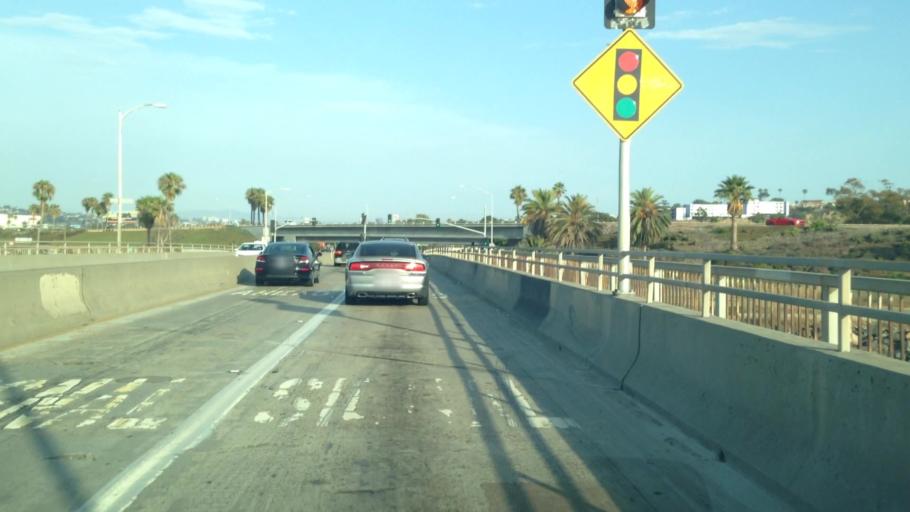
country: US
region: California
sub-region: San Diego County
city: San Diego
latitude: 32.7581
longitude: -117.2250
